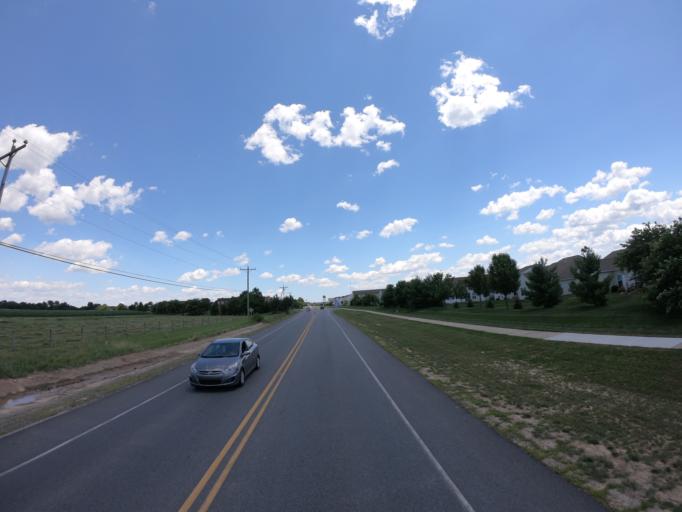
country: US
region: Delaware
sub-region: New Castle County
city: Middletown
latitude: 39.4542
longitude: -75.7379
